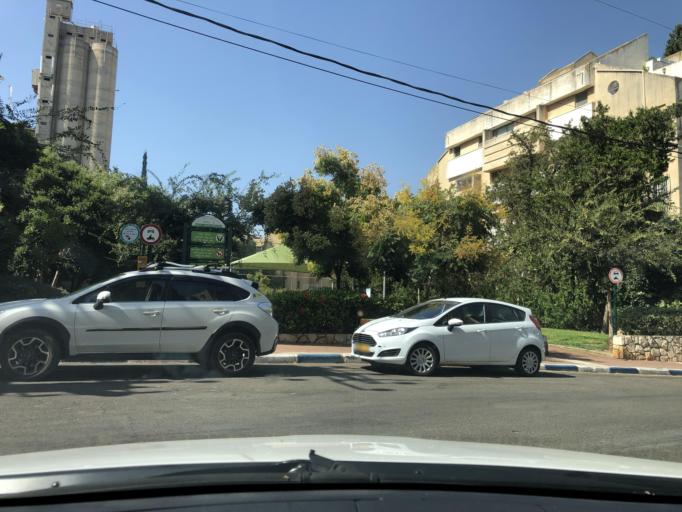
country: IL
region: Central District
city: Kfar Saba
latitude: 32.1740
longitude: 34.8943
